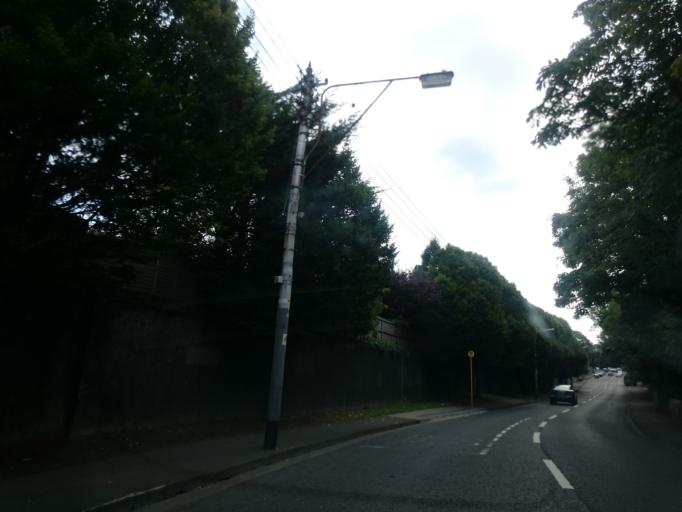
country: IE
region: Leinster
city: Rathmines
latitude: 53.3089
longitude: -6.2600
